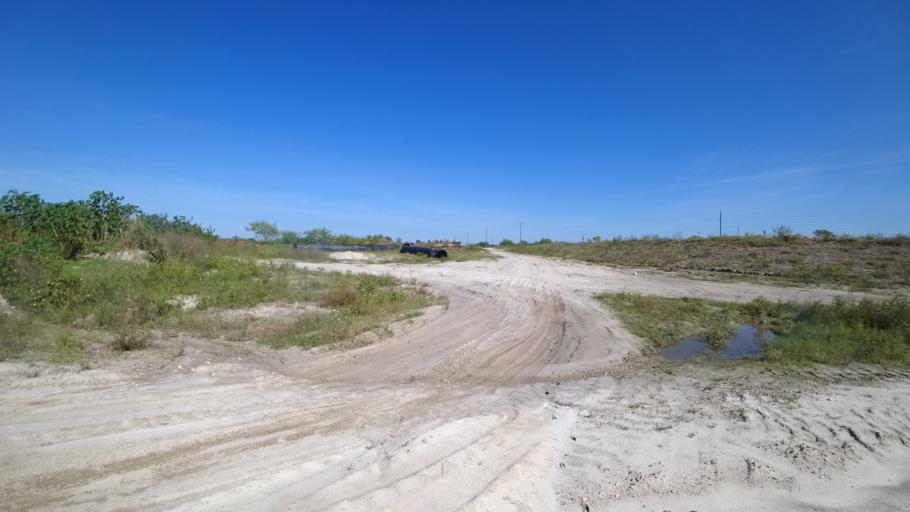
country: US
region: Florida
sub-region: Hillsborough County
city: Balm
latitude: 27.6481
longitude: -82.0743
